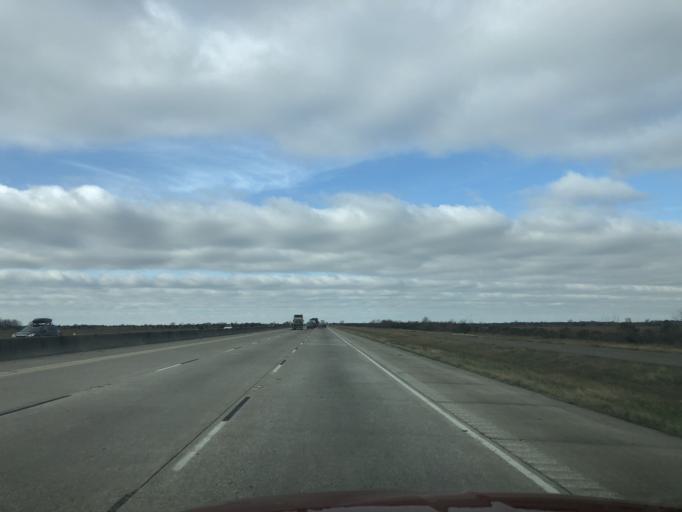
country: US
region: Texas
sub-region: Chambers County
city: Winnie
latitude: 29.8278
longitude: -94.4493
